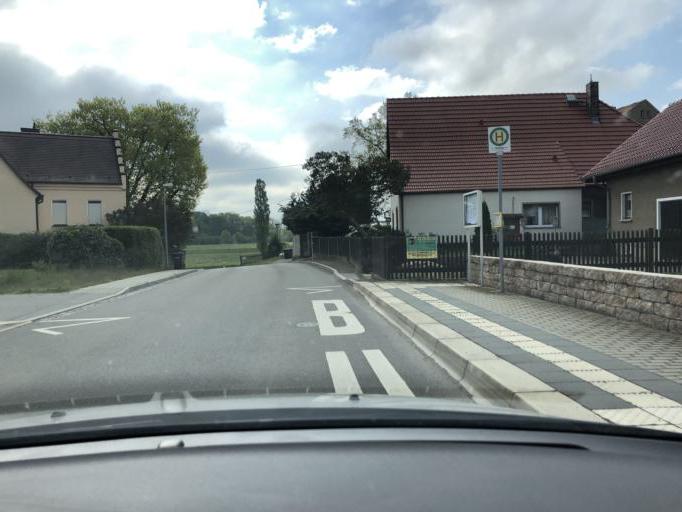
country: DE
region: Thuringia
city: Haselbach
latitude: 51.0542
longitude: 12.4403
